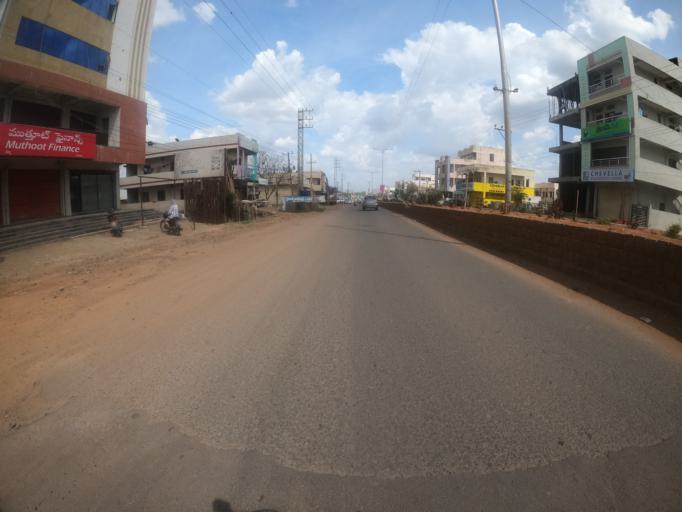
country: IN
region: Telangana
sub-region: Rangareddi
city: Sriramnagar
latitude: 17.3103
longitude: 78.1417
